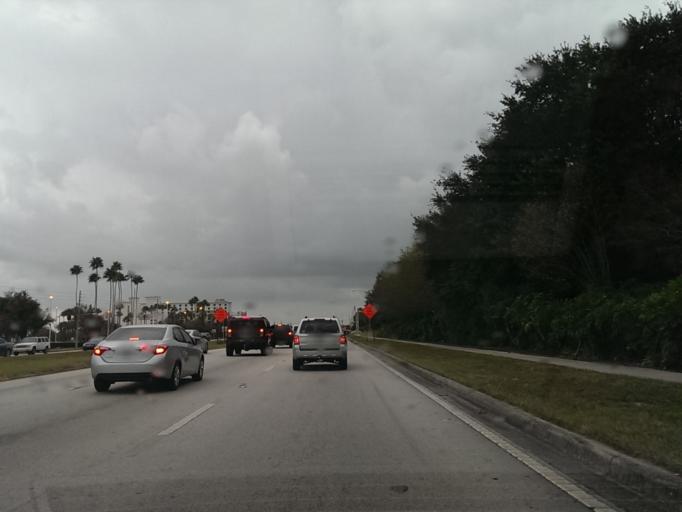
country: US
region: Florida
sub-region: Orange County
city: Tangelo Park
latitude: 28.4811
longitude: -81.4590
